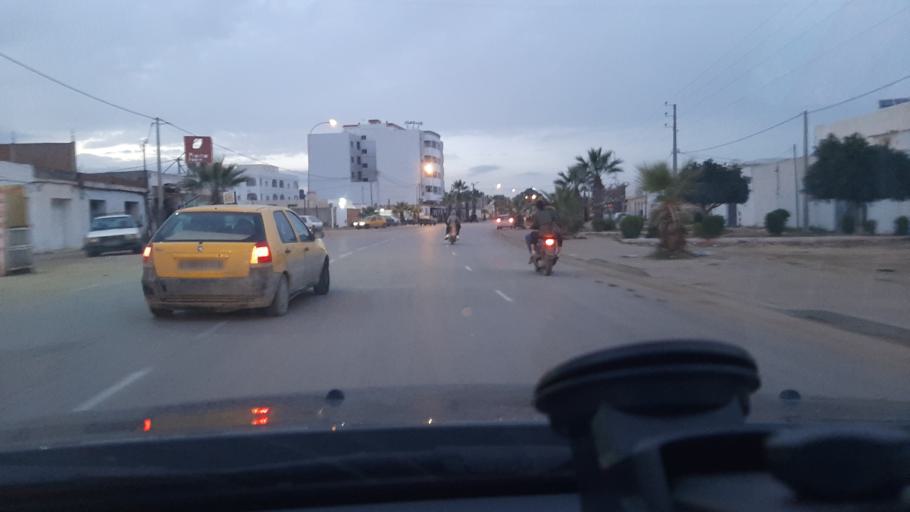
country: TN
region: Safaqis
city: Sfax
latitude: 34.7640
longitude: 10.6895
